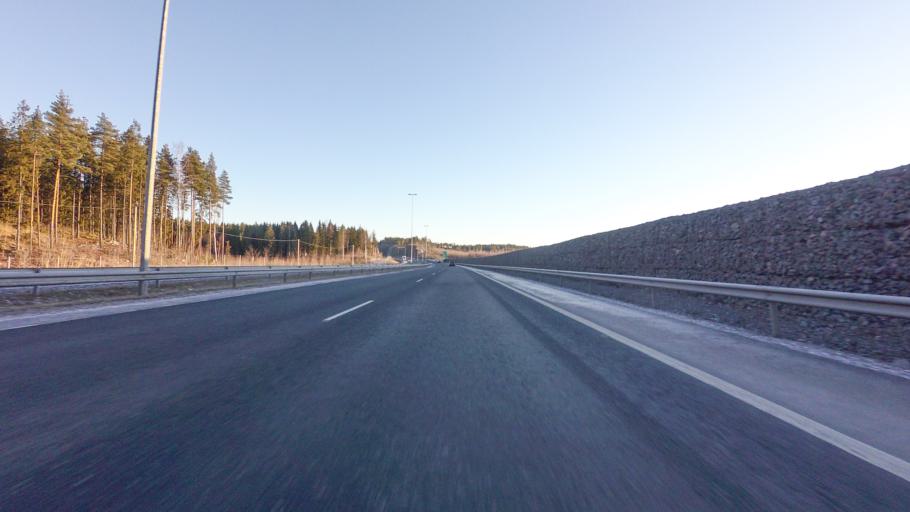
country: FI
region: Uusimaa
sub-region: Helsinki
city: Lohja
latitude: 60.2854
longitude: 24.0901
